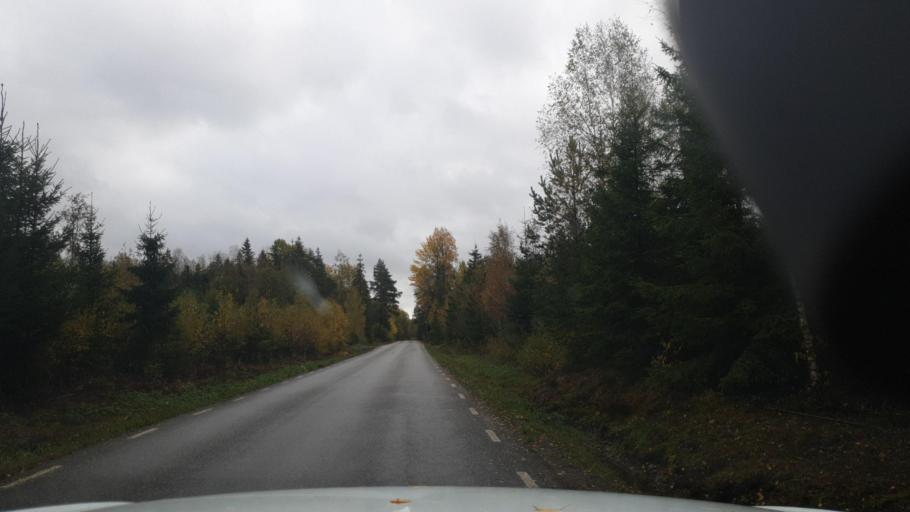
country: SE
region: Vaermland
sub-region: Karlstads Kommun
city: Valberg
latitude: 59.4184
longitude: 13.1173
